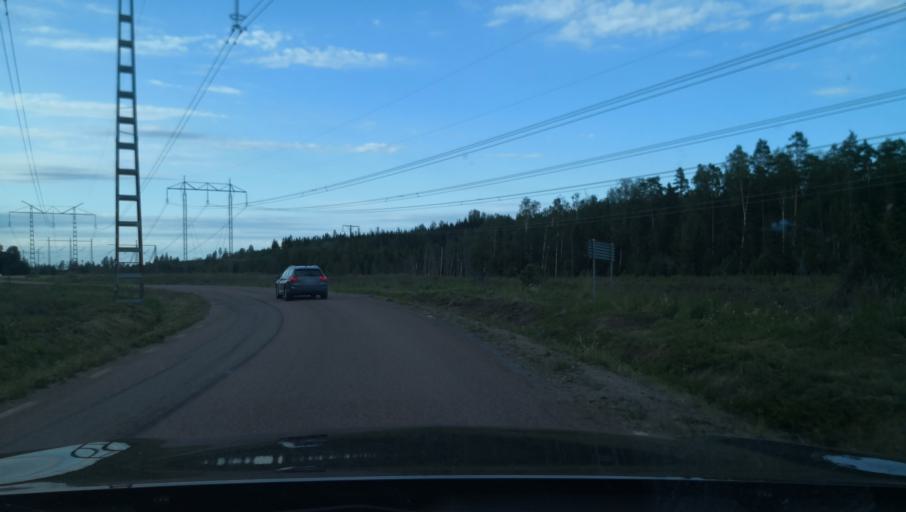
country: SE
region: Dalarna
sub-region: Ludvika Kommun
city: Ludvika
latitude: 60.0934
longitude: 15.2694
